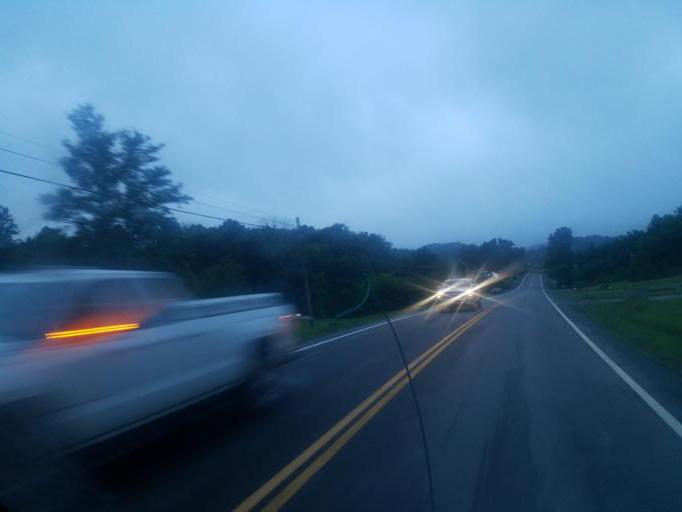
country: US
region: Ohio
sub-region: Carroll County
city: Carrollton
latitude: 40.5495
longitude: -81.0458
